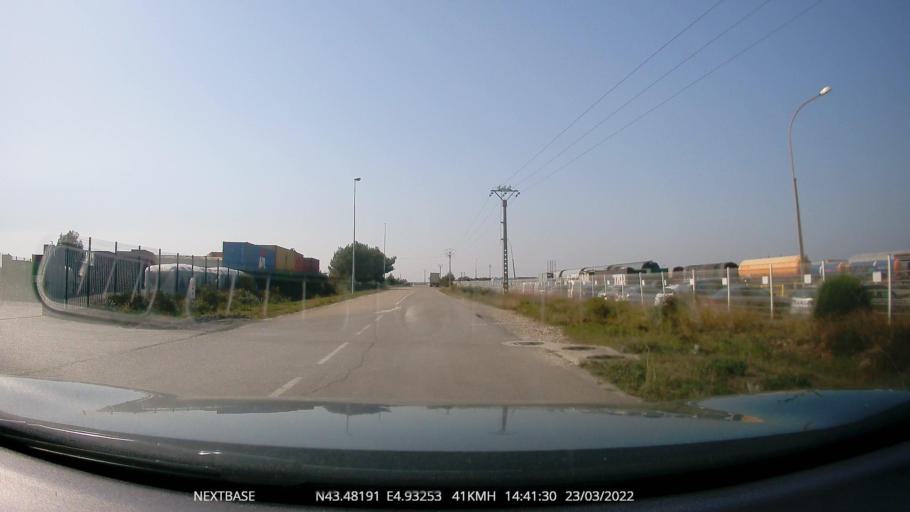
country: FR
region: Provence-Alpes-Cote d'Azur
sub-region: Departement des Bouches-du-Rhone
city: Fos-sur-Mer
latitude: 43.4819
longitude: 4.9327
